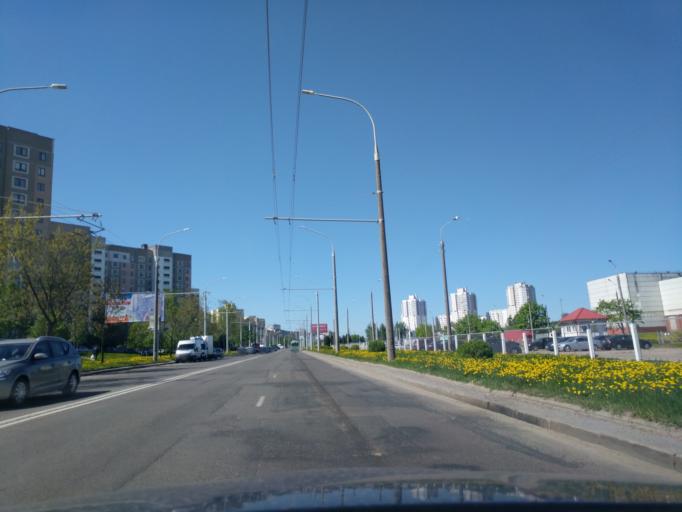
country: BY
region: Minsk
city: Novoye Medvezhino
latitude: 53.8820
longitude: 27.4524
